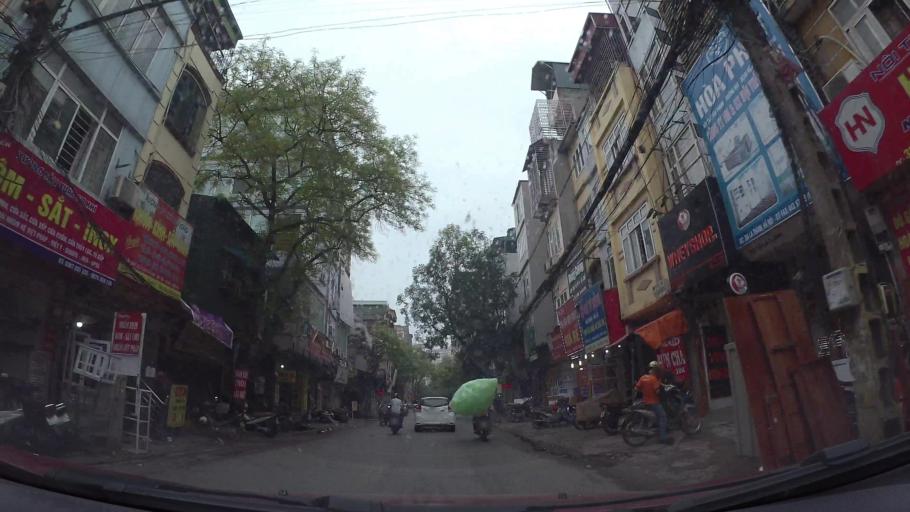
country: VN
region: Ha Noi
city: Dong Da
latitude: 21.0222
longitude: 105.8238
